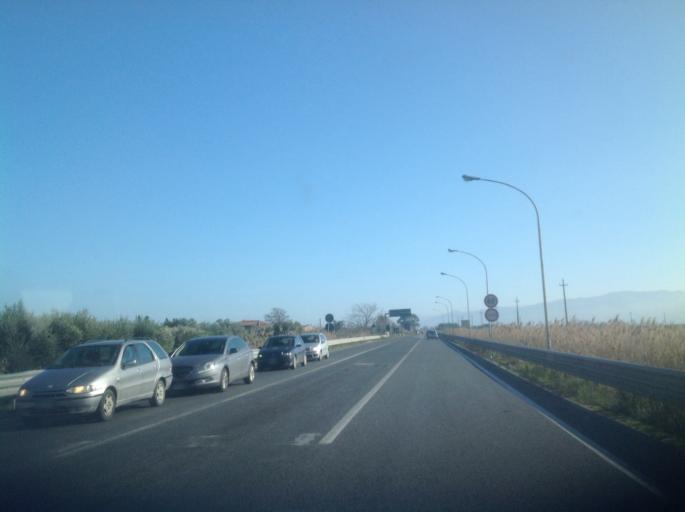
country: IT
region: Calabria
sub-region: Provincia di Cosenza
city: Sibari
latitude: 39.7263
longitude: 16.4840
